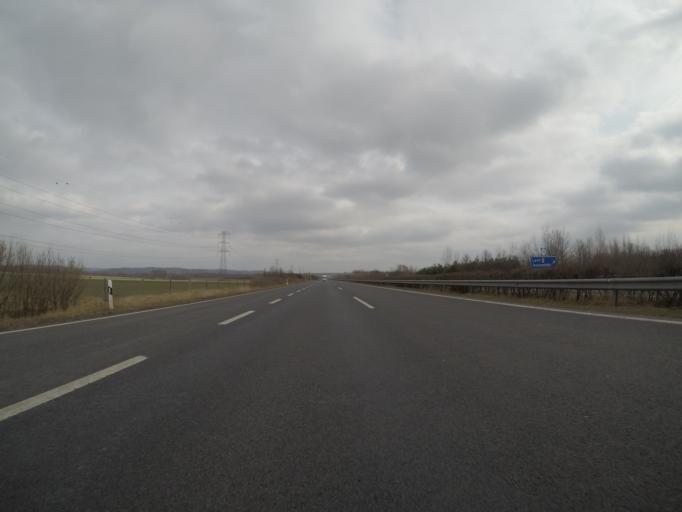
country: HR
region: Medimurska
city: Podturen
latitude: 46.5103
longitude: 16.5576
